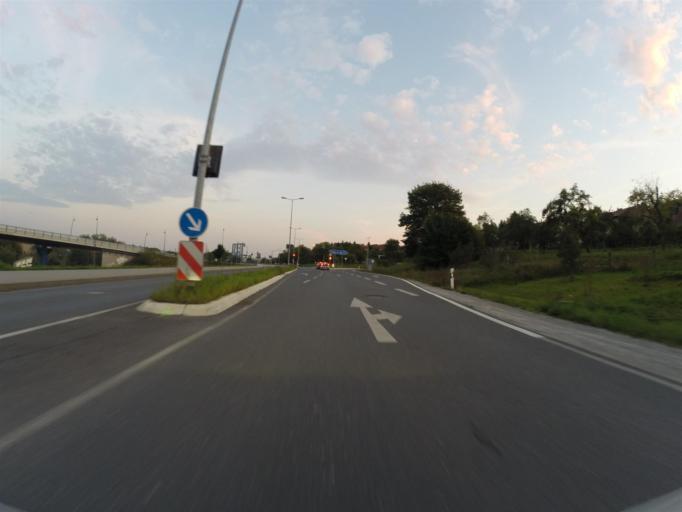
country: DE
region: Thuringia
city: Sulza
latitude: 50.8777
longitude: 11.5931
